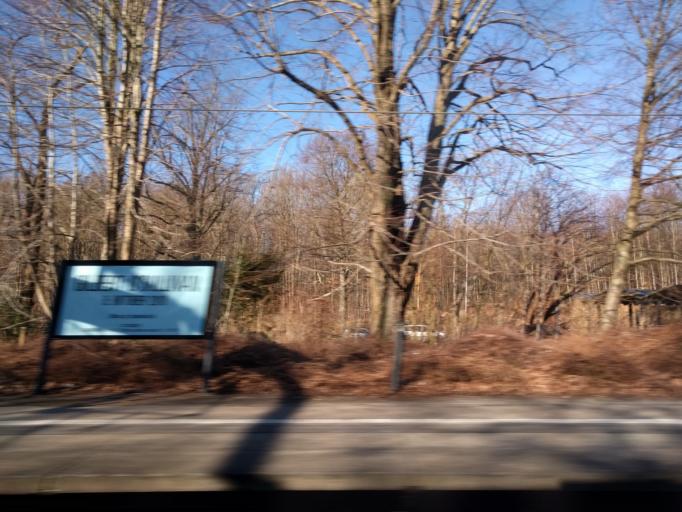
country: DK
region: Capital Region
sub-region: Rudersdal Kommune
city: Trorod
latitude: 55.8231
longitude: 12.5715
